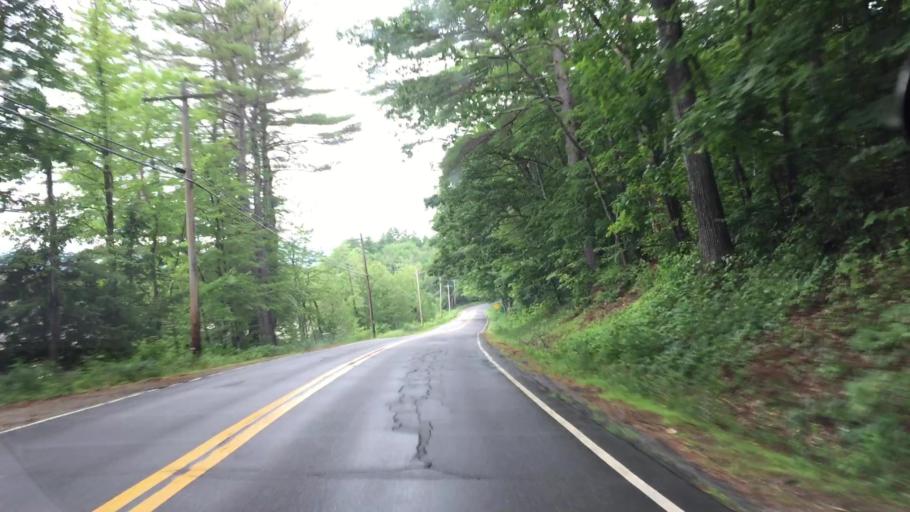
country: US
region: New Hampshire
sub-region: Carroll County
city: Center Harbor
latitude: 43.7512
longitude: -71.4812
